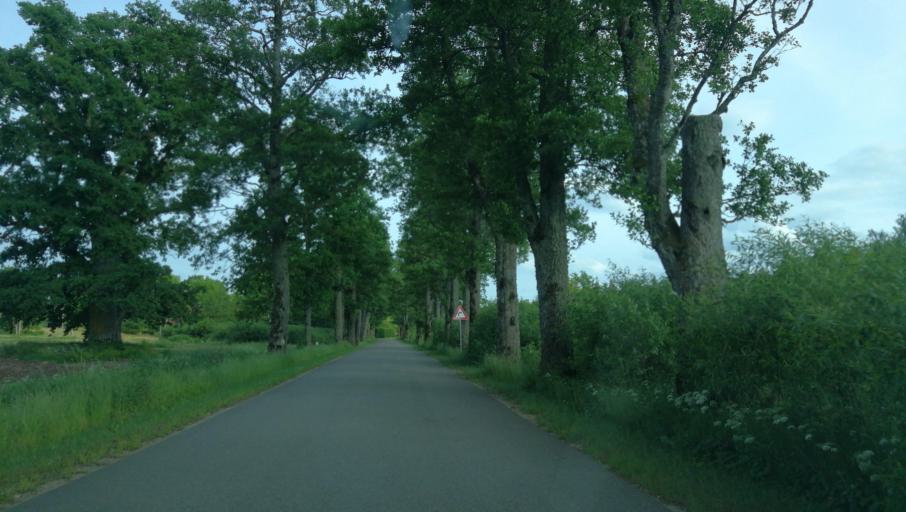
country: LV
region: Pargaujas
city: Stalbe
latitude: 57.3556
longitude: 25.0913
